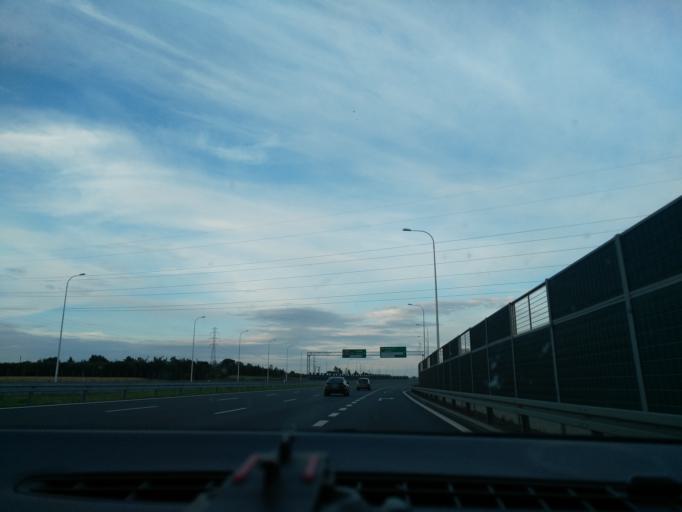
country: PL
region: Lublin Voivodeship
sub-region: Powiat lubelski
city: Lublin
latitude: 51.3024
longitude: 22.5709
